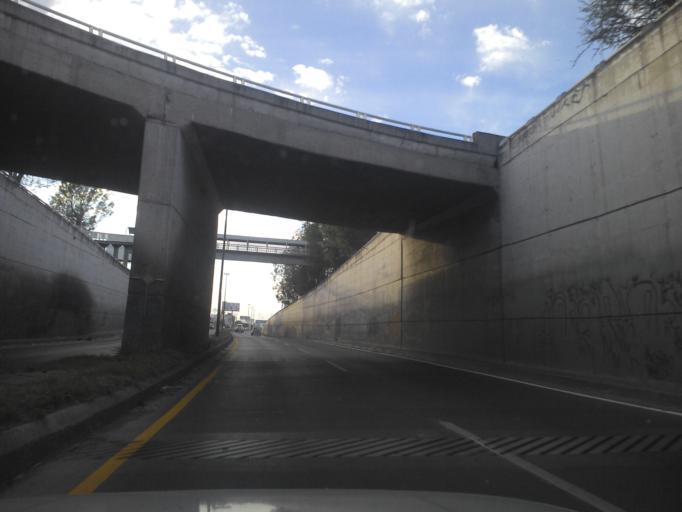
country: MX
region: Jalisco
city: Tlaquepaque
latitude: 20.6163
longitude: -103.2851
